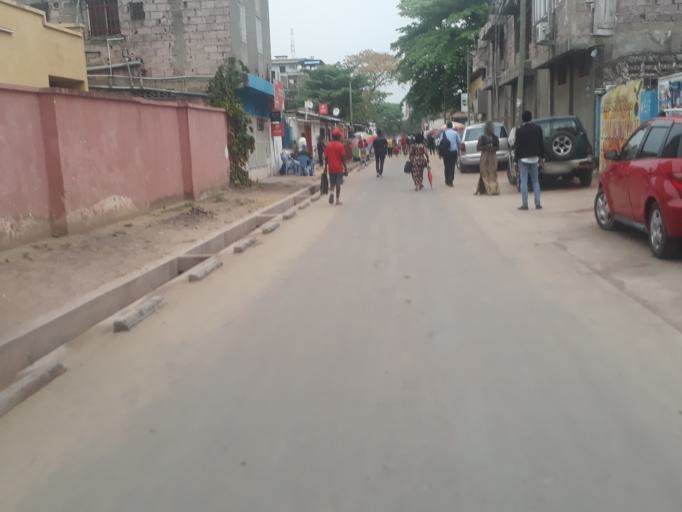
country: CD
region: Kinshasa
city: Kinshasa
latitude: -4.3086
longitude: 15.2984
